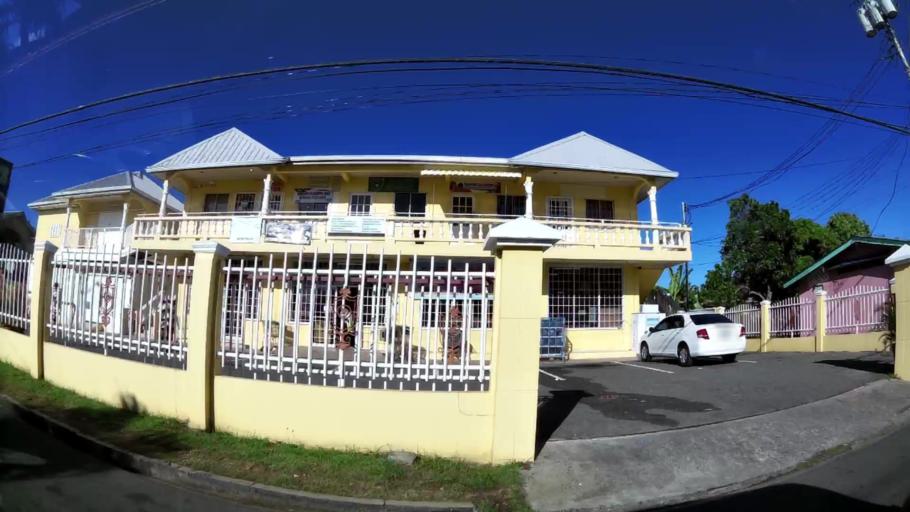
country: TT
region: Tobago
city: Scarborough
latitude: 11.1571
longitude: -60.8205
